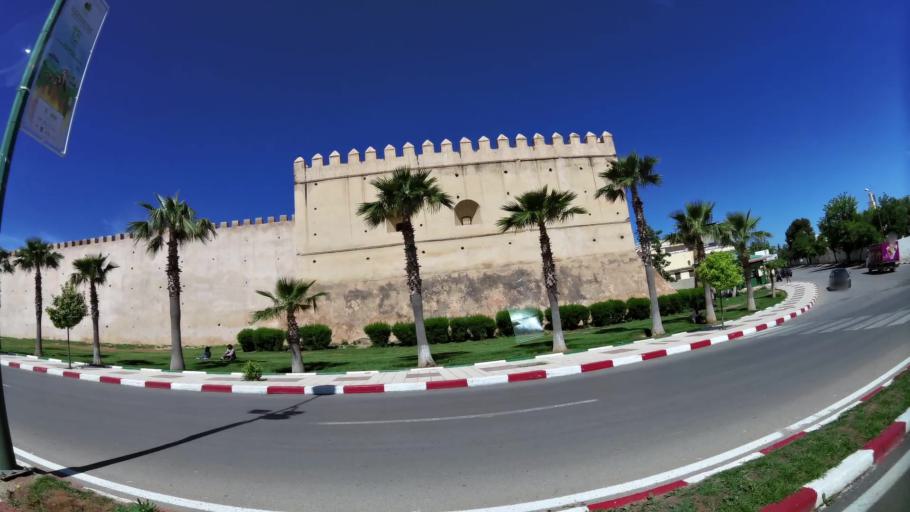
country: MA
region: Meknes-Tafilalet
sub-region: Meknes
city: Meknes
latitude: 33.8873
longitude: -5.5528
